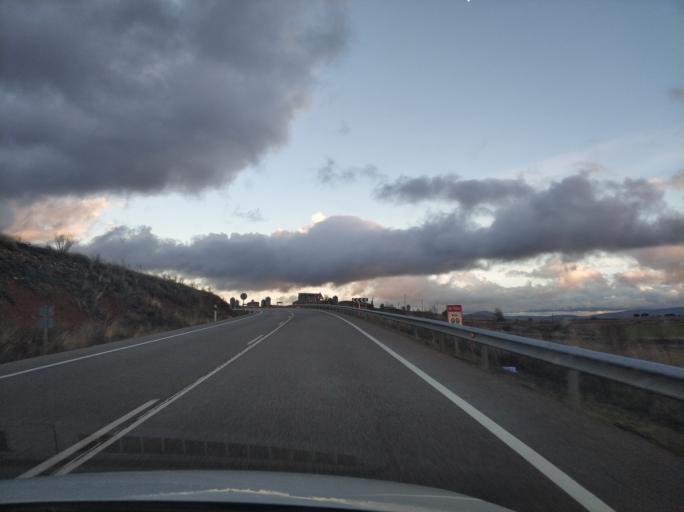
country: ES
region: Castille and Leon
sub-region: Provincia de Segovia
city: Ayllon
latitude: 41.4147
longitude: -3.4006
